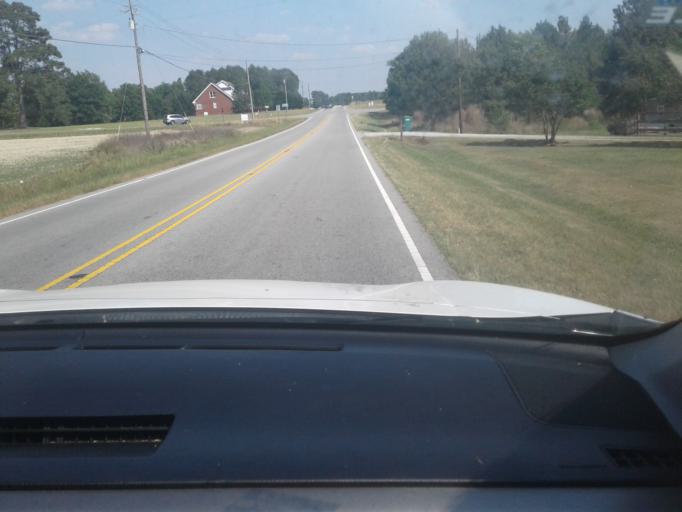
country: US
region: North Carolina
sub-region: Johnston County
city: Benson
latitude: 35.3972
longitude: -78.5974
